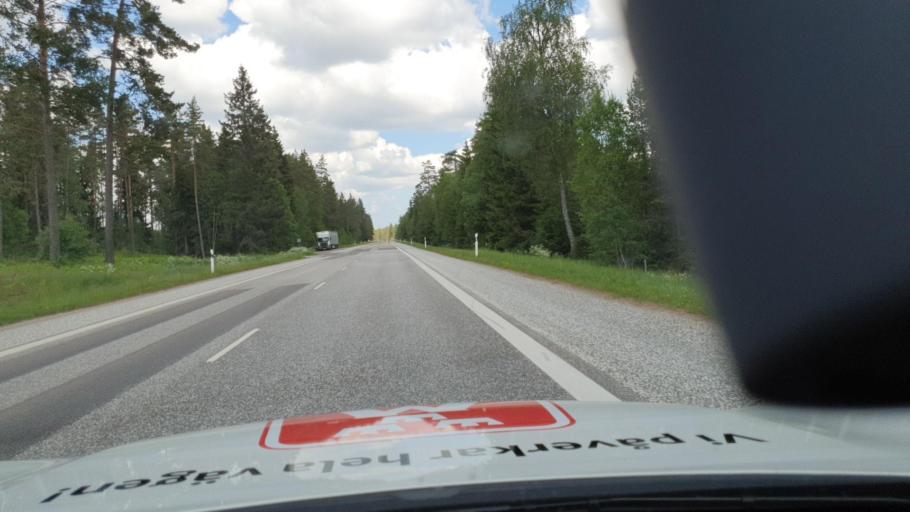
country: SE
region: Joenkoeping
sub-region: Jonkopings Kommun
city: Odensjo
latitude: 57.6284
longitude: 14.2037
